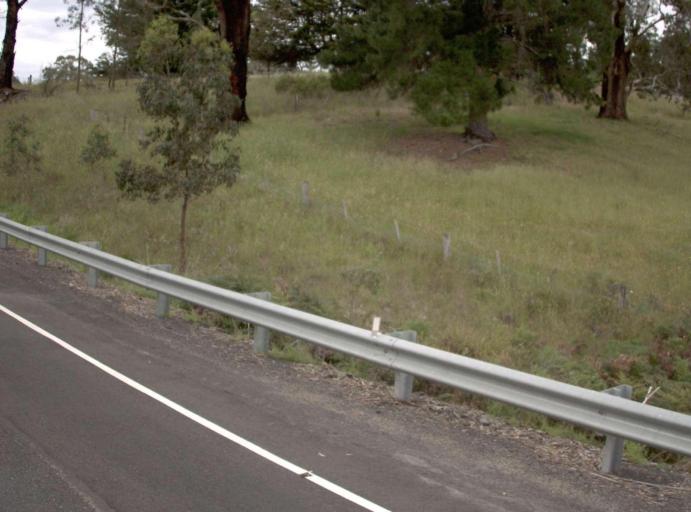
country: AU
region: New South Wales
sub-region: Bombala
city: Bombala
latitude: -37.4842
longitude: 149.1804
